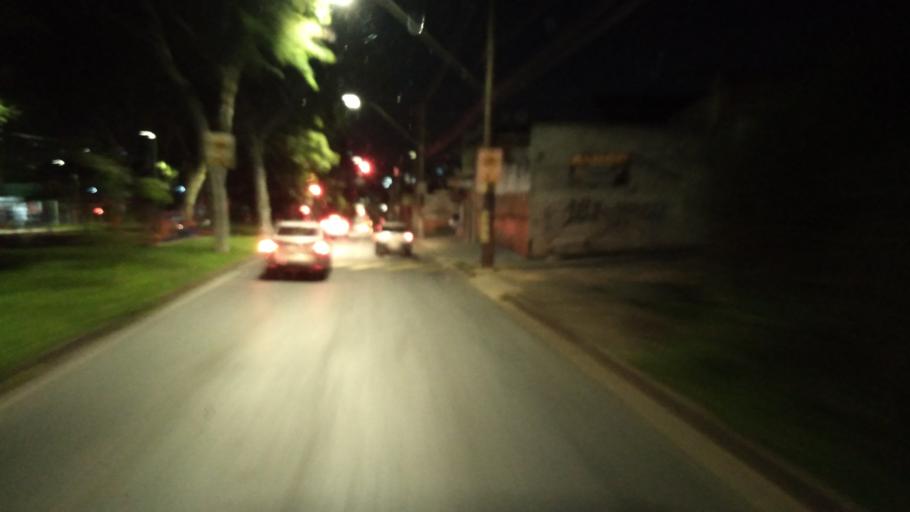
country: BR
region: Minas Gerais
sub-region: Belo Horizonte
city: Belo Horizonte
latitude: -19.8765
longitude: -43.9101
